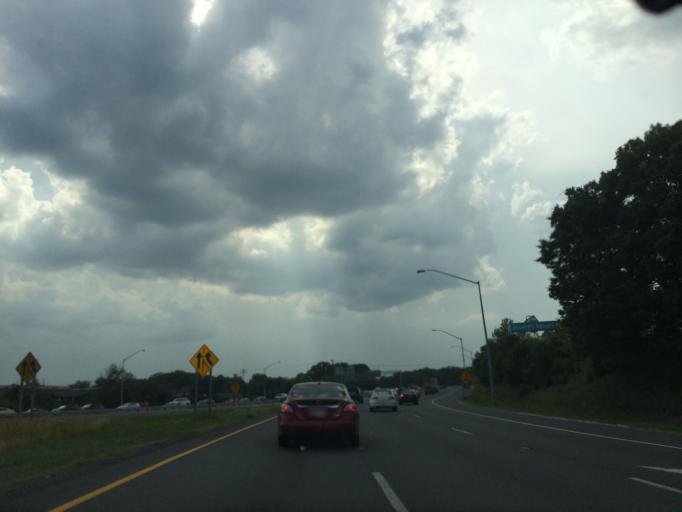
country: US
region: Maryland
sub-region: Baltimore County
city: Woodlawn
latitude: 39.3067
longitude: -76.7501
